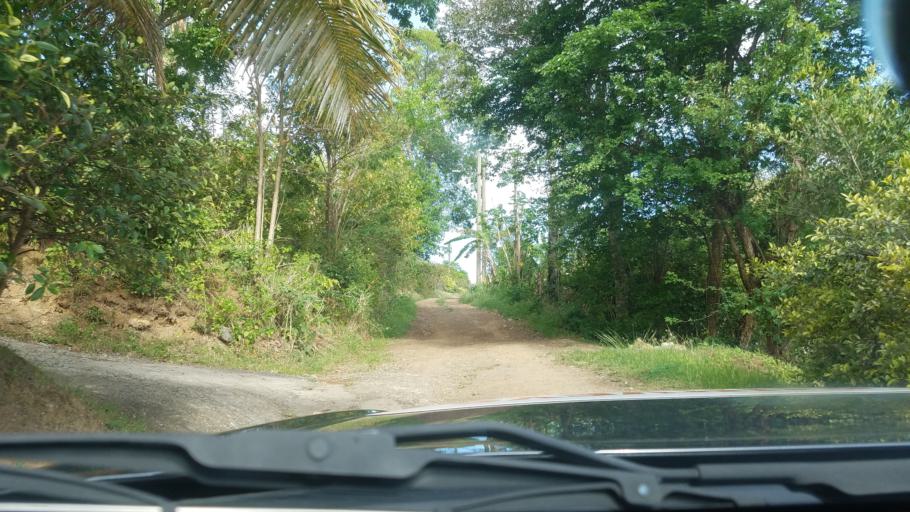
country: LC
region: Gros-Islet
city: Gros Islet
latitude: 14.0631
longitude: -60.9580
